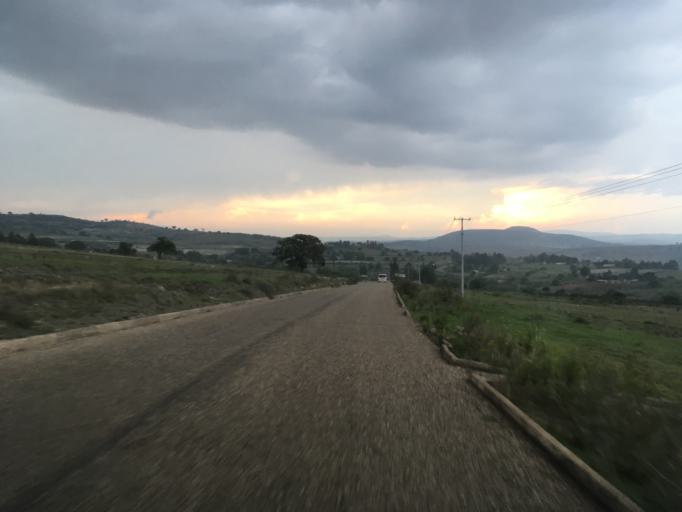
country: MX
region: Oaxaca
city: Santiago Tilantongo
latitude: 17.2818
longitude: -97.2903
